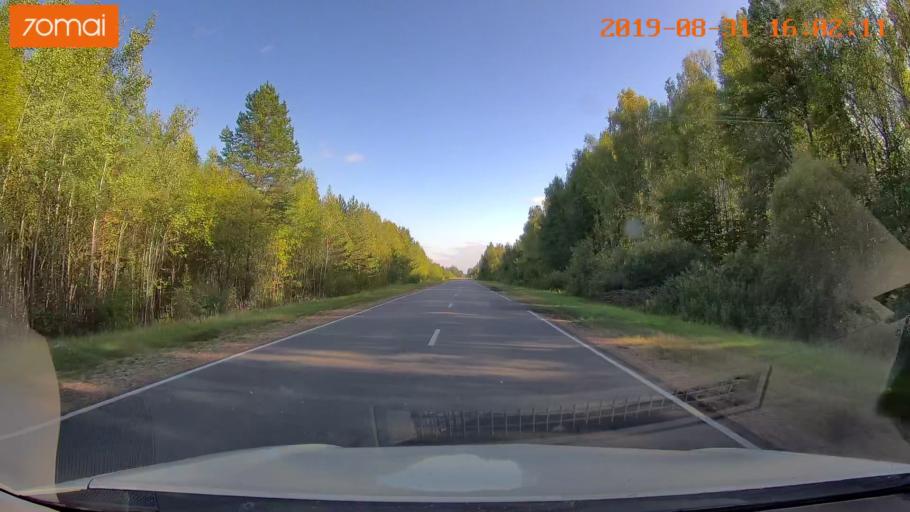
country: RU
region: Kaluga
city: Yukhnov
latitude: 54.6785
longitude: 35.2986
